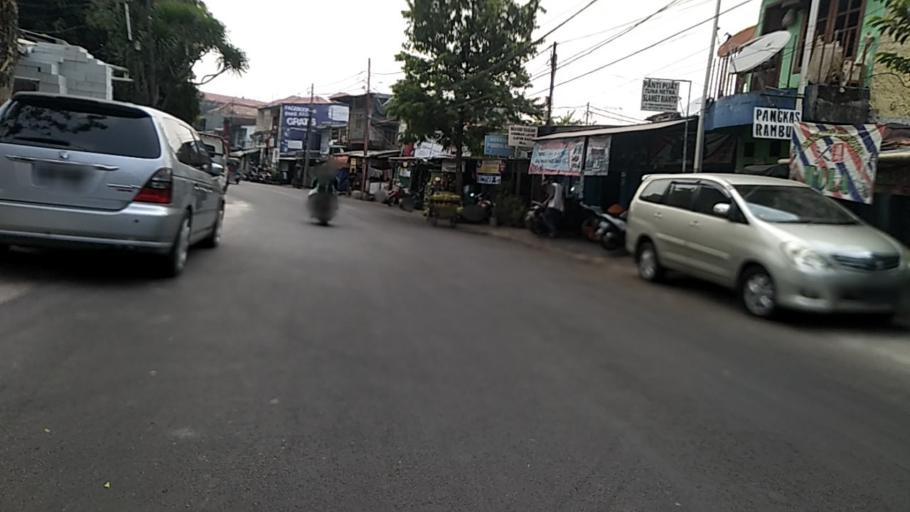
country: ID
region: Jakarta Raya
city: Jakarta
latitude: -6.2322
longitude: 106.8513
